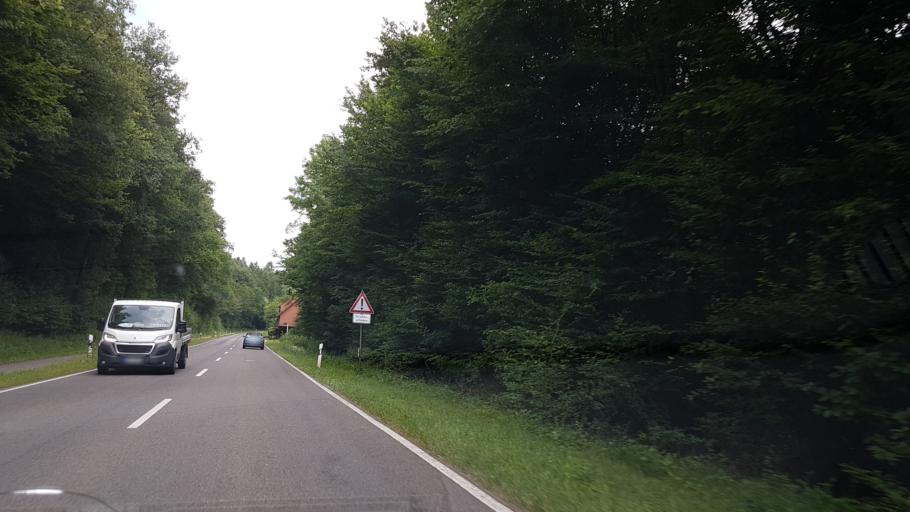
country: DE
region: Saarland
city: Quierschied
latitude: 49.2958
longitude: 7.0171
